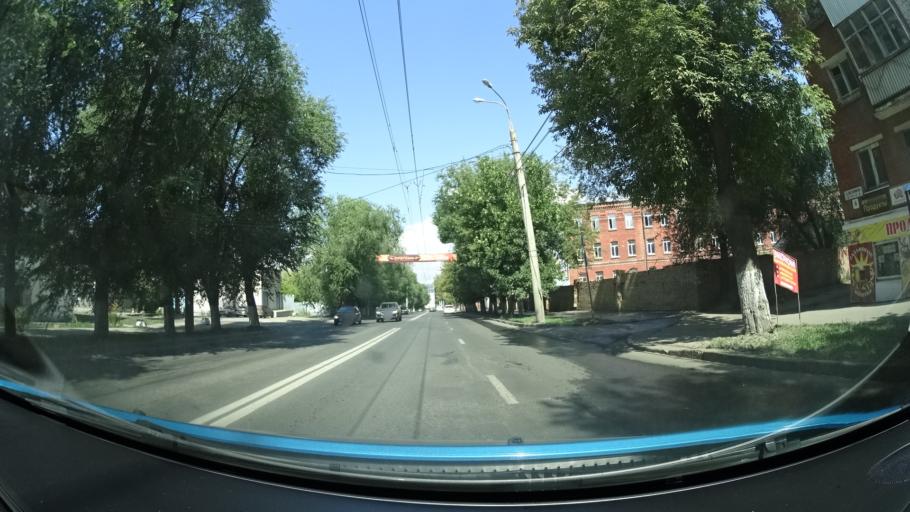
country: RU
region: Samara
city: Samara
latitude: 53.2134
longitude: 50.1530
